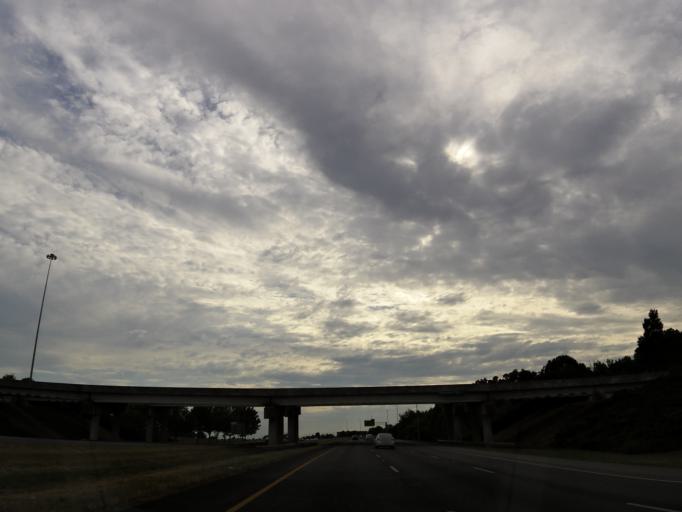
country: US
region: Alabama
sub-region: Madison County
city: Madison
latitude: 34.6667
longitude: -86.7702
